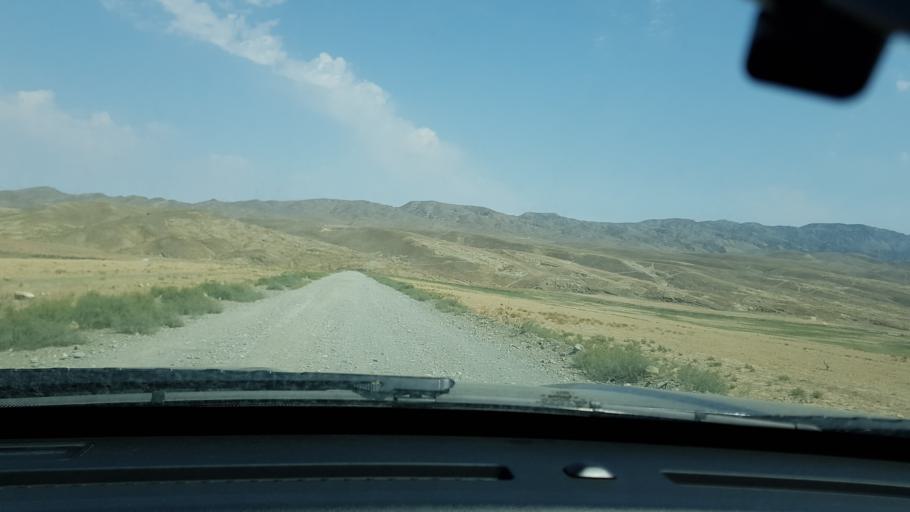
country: TM
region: Ahal
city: Baharly
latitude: 38.4117
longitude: 57.0159
